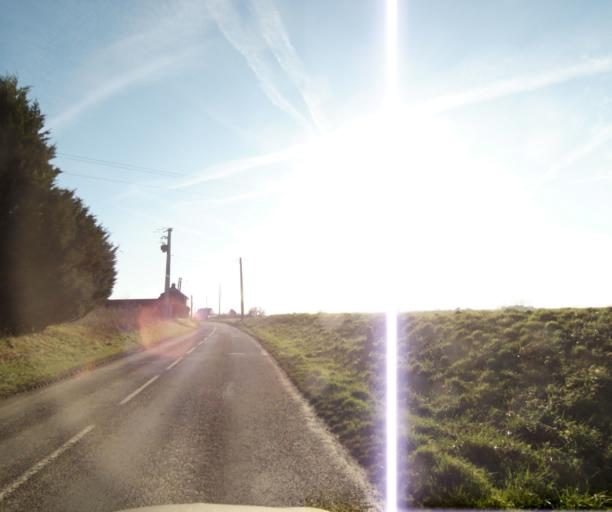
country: FR
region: Nord-Pas-de-Calais
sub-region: Departement du Nord
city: Saultain
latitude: 50.3298
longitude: 3.5751
